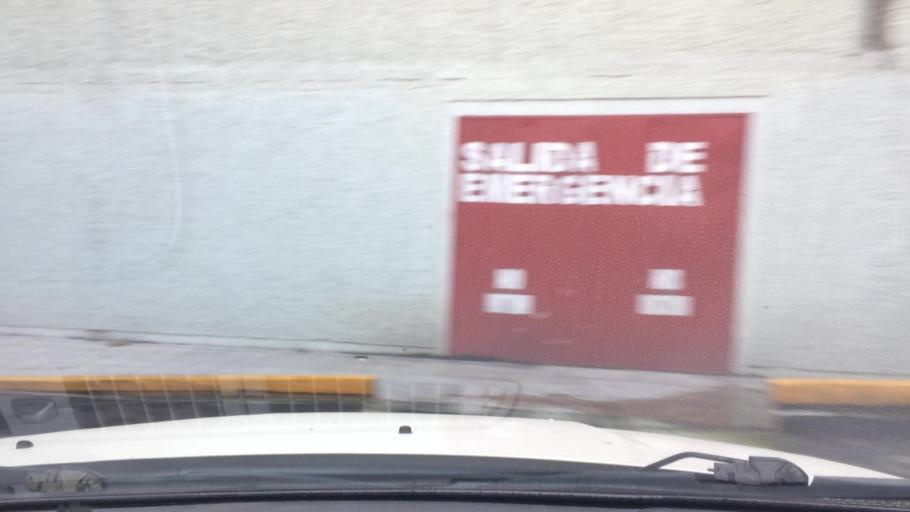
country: MX
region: Mexico City
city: Colonia del Valle
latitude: 19.3842
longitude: -99.1895
